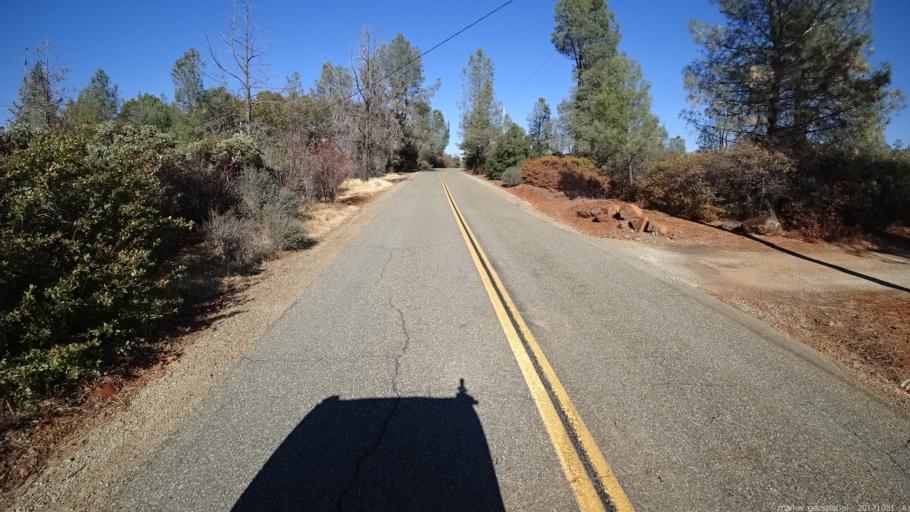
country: US
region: California
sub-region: Shasta County
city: Shingletown
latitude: 40.4957
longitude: -121.9970
